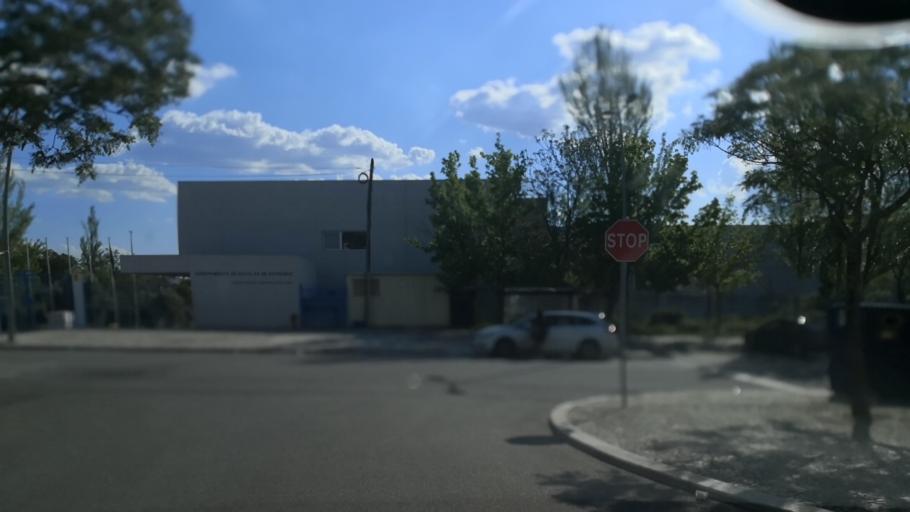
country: PT
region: Evora
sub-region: Estremoz
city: Estremoz
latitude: 38.8489
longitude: -7.5888
